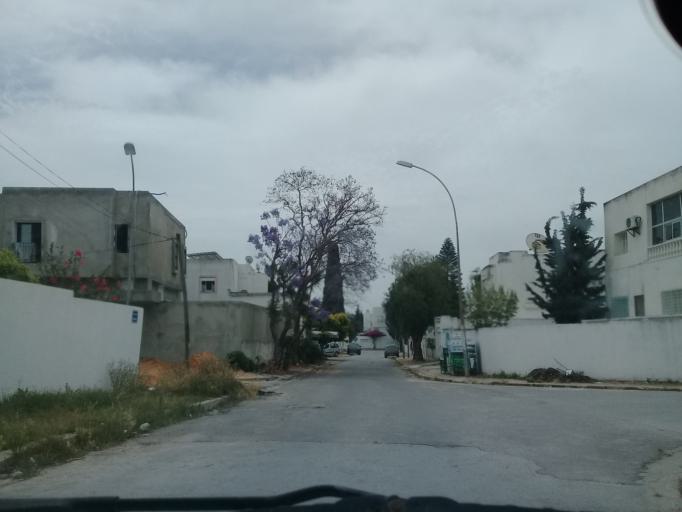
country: TN
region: Tunis
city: Tunis
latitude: 36.8405
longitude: 10.1647
